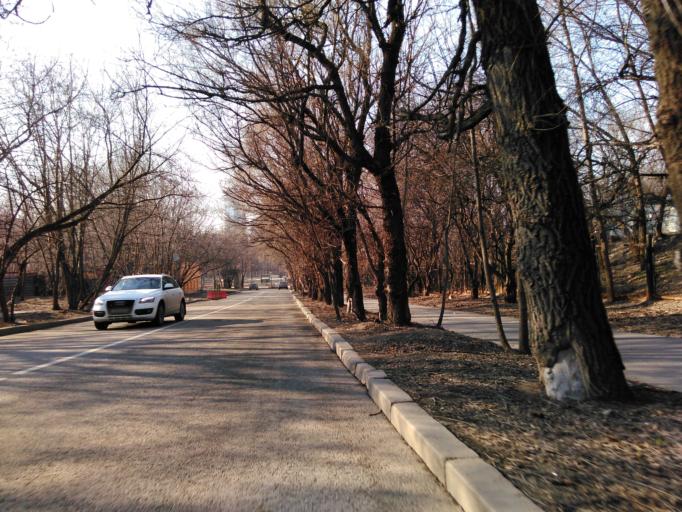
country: RU
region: Moscow
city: Vorob'yovo
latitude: 55.7071
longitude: 37.5207
